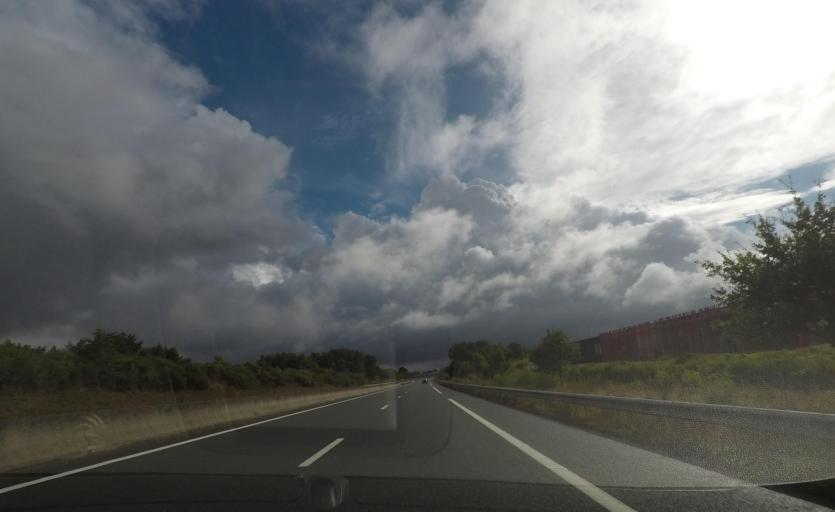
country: FR
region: Pays de la Loire
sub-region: Departement de la Vendee
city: La Ferriere
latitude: 46.6663
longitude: -1.3627
